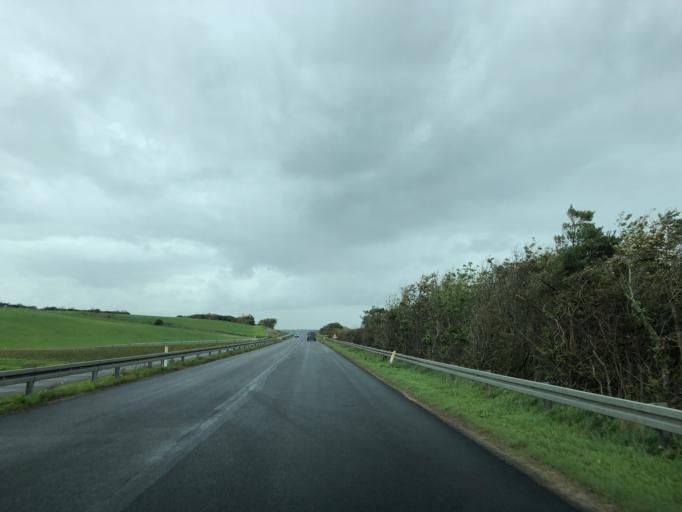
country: DK
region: Central Jutland
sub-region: Struer Kommune
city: Struer
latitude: 56.5501
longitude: 8.5589
